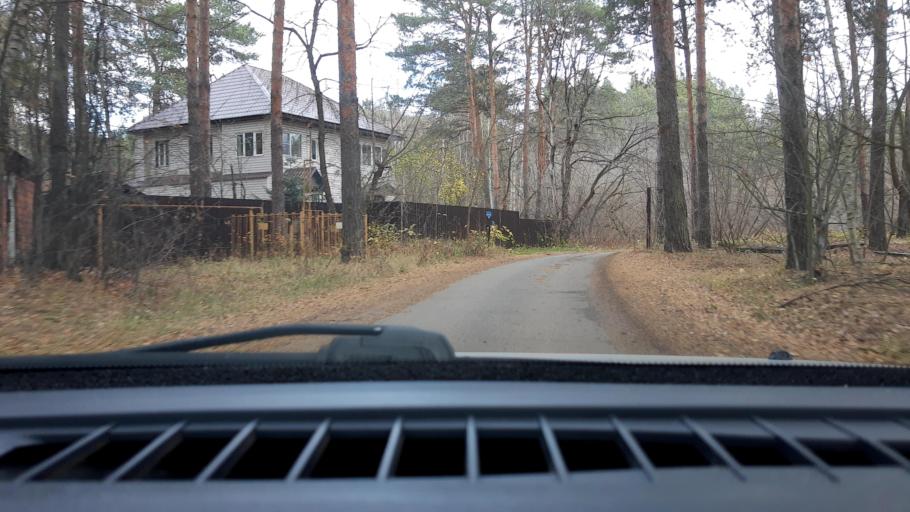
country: RU
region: Nizjnij Novgorod
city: Kstovo
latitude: 56.1681
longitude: 44.1212
